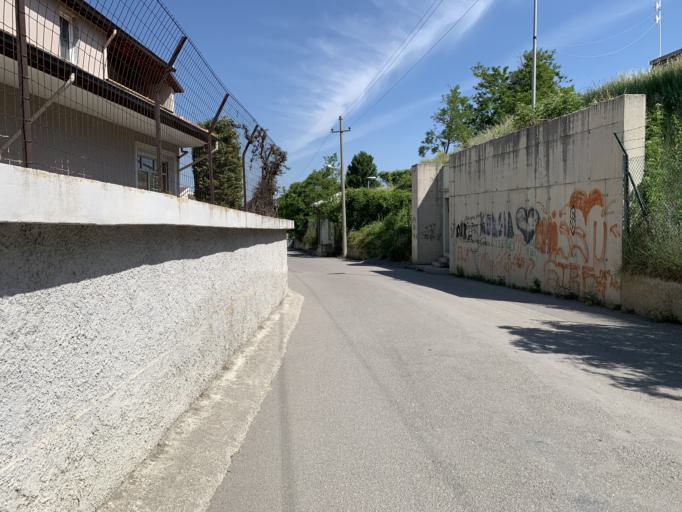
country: AL
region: Korce
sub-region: Rrethi i Korces
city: Korce
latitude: 40.6181
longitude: 20.7870
